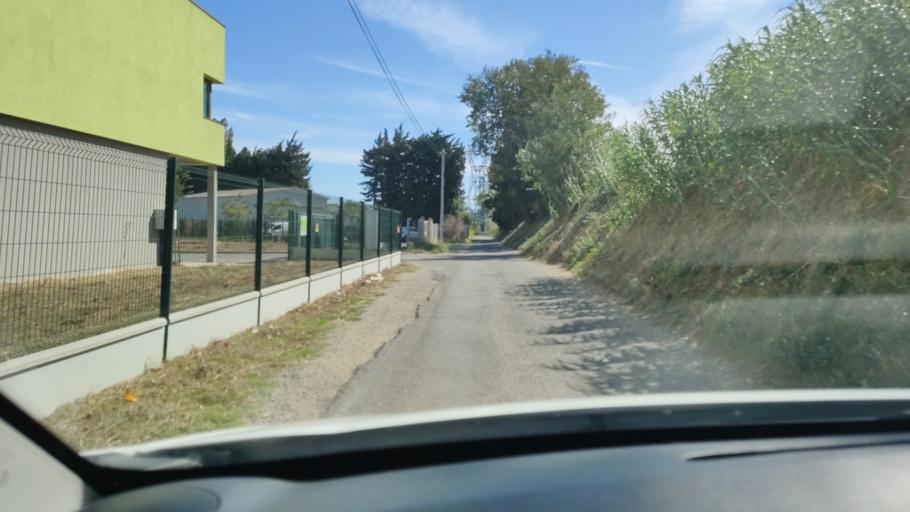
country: FR
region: Provence-Alpes-Cote d'Azur
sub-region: Departement du Vaucluse
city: Morieres-les-Avignon
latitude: 43.9518
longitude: 4.8857
